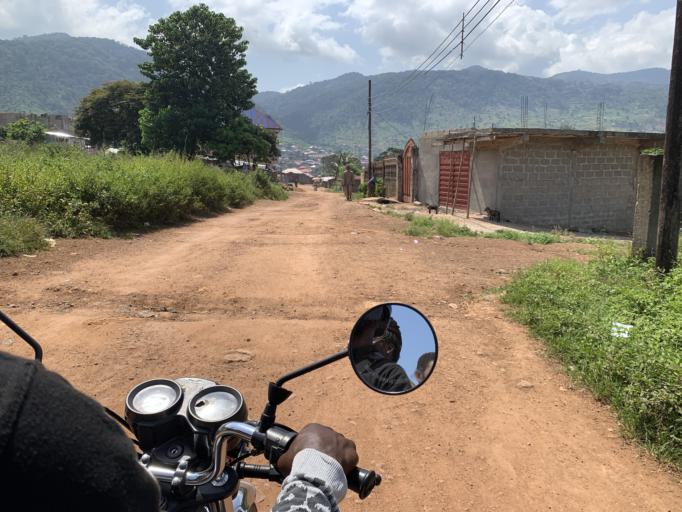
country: SL
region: Western Area
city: Hastings
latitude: 8.3809
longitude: -13.1463
